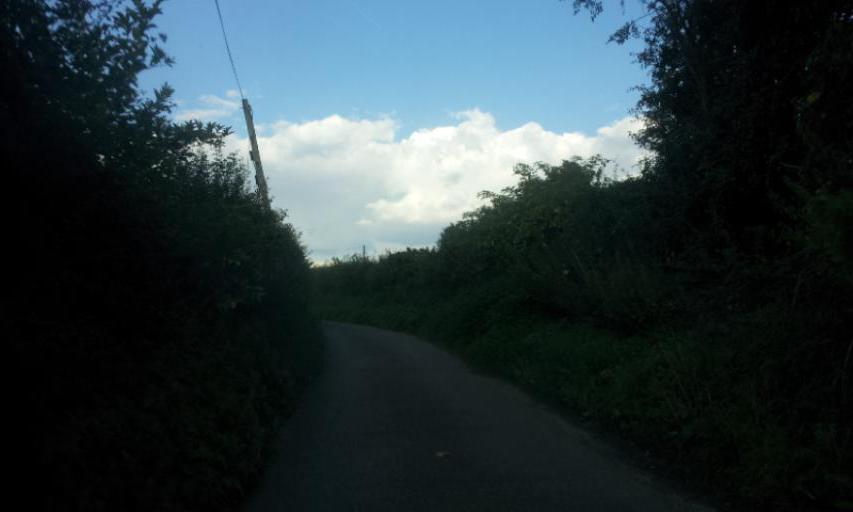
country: GB
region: England
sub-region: Kent
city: Longfield
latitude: 51.4063
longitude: 0.2644
